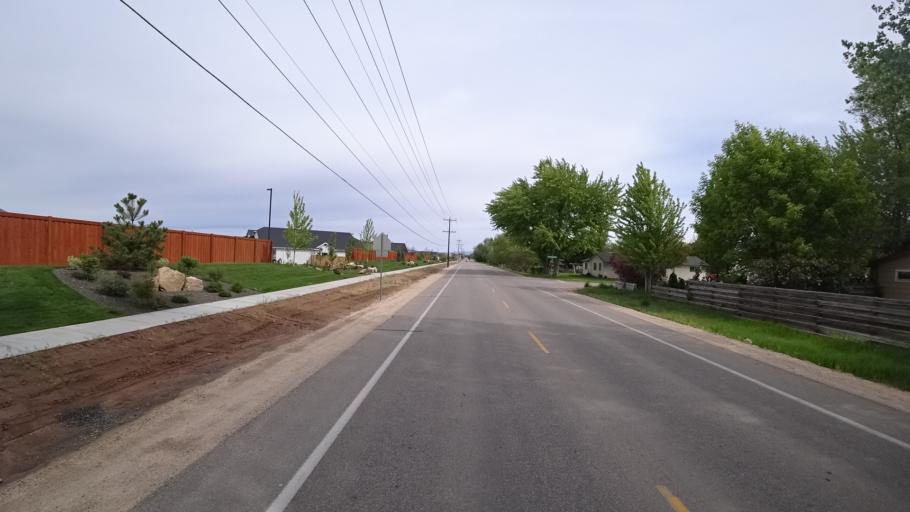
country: US
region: Idaho
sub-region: Ada County
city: Meridian
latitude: 43.5398
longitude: -116.3145
